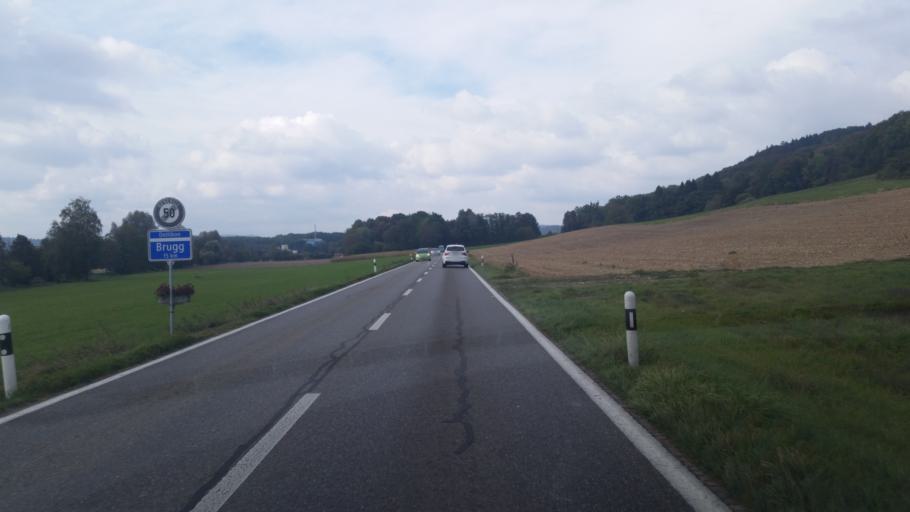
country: CH
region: Aargau
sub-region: Bezirk Bremgarten
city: Hagglingen
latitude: 47.3674
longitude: 8.2589
